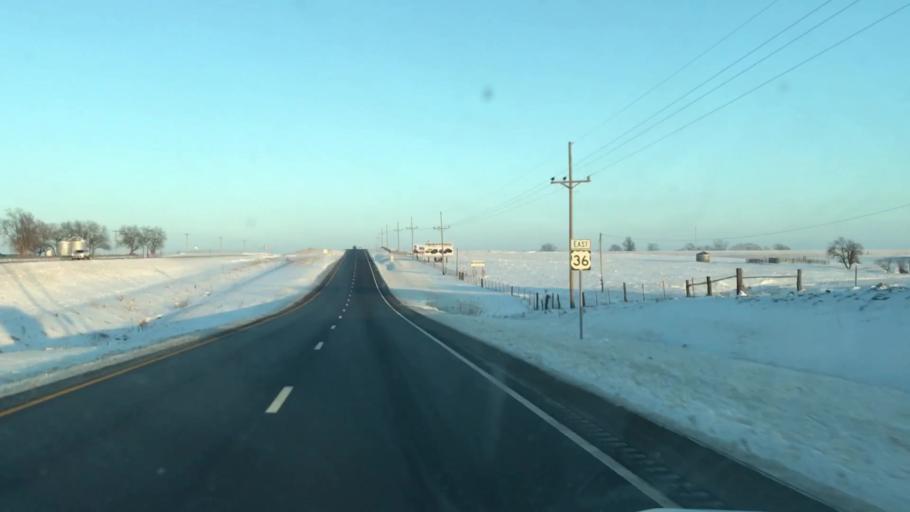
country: US
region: Missouri
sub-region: Clinton County
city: Cameron
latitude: 39.7541
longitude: -94.2807
